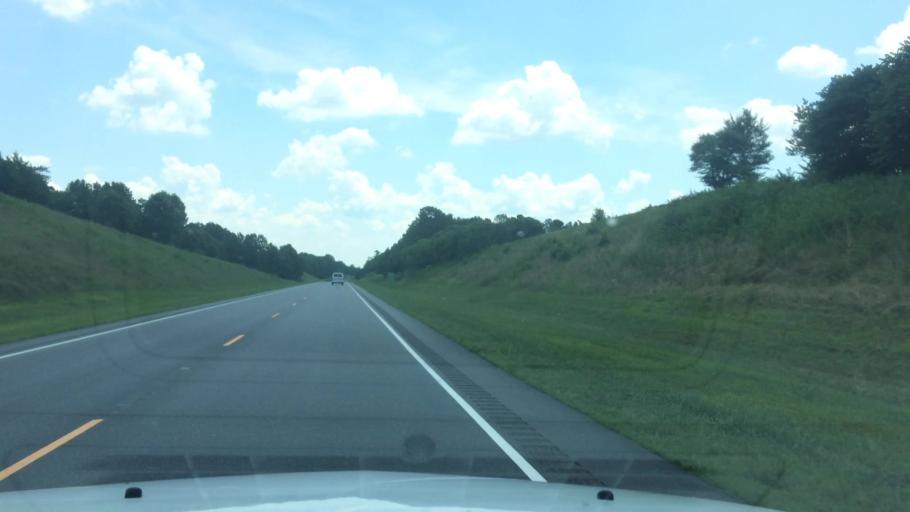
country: US
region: North Carolina
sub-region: Alexander County
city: Stony Point
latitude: 35.8804
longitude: -81.0725
